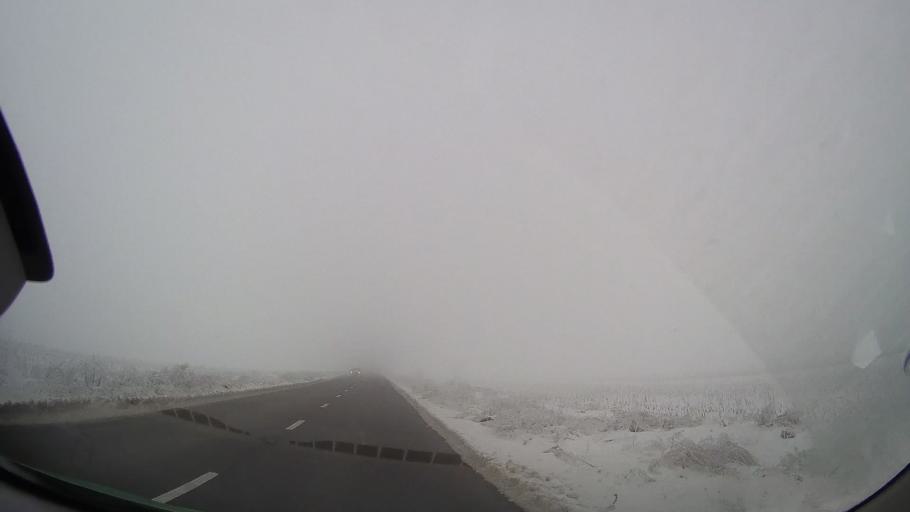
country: RO
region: Iasi
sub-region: Comuna Mircesti
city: Iugani
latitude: 47.0413
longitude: 26.8512
